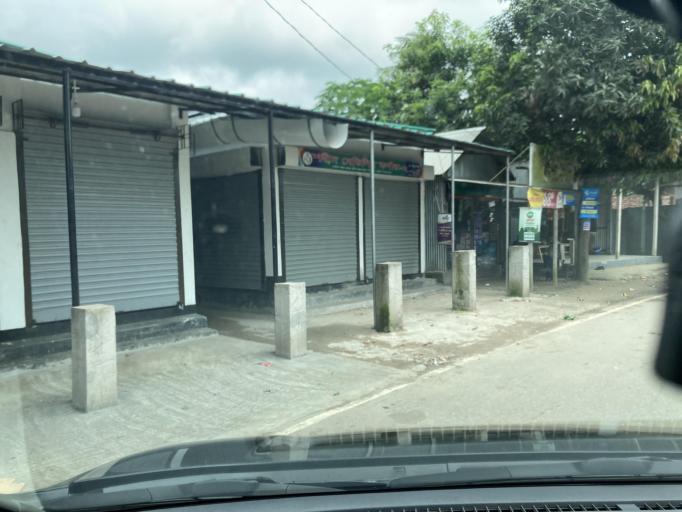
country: BD
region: Dhaka
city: Dohar
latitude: 23.7639
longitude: 90.1912
